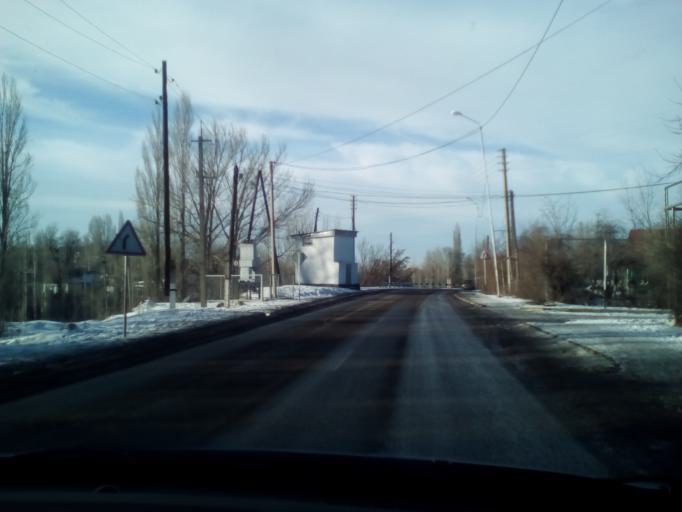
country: KZ
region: Almaty Oblysy
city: Burunday
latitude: 43.1593
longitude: 76.4178
